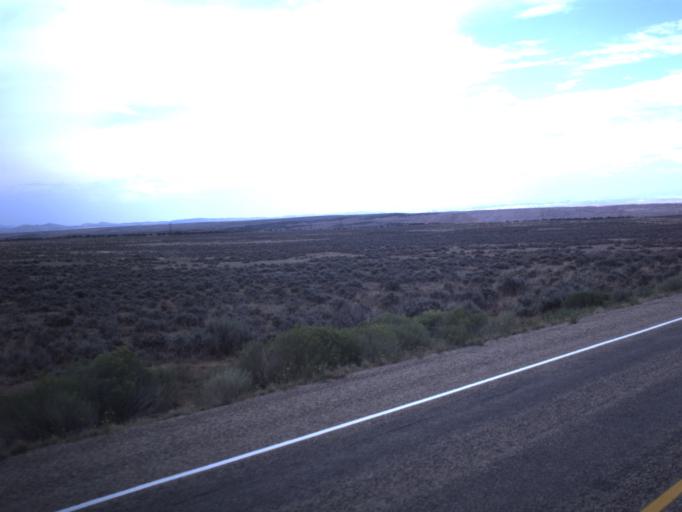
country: US
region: Utah
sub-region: Uintah County
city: Naples
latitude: 40.1508
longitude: -109.2991
